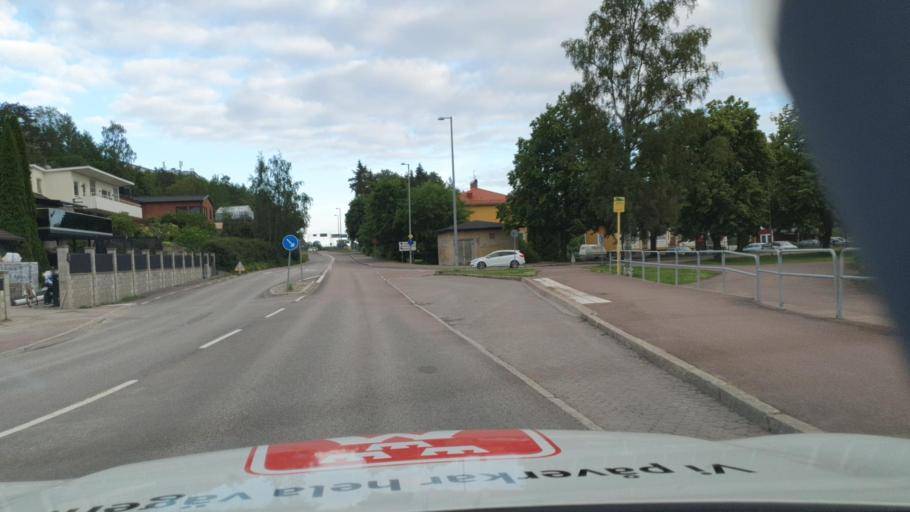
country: SE
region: Vaermland
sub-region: Karlstads Kommun
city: Karlstad
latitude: 59.3995
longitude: 13.5145
